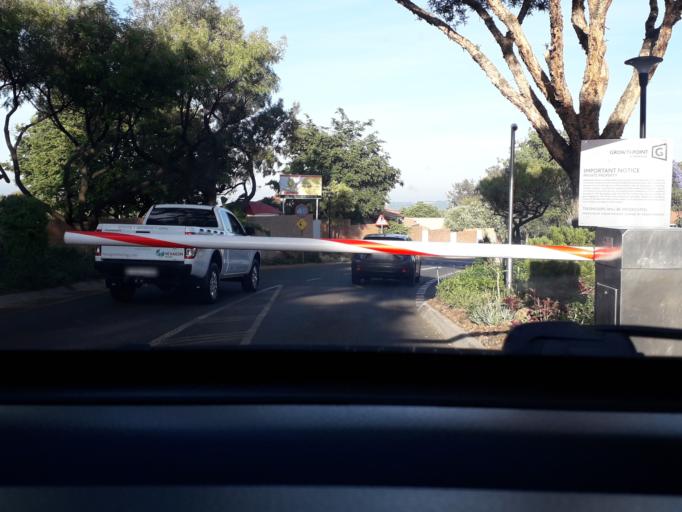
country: ZA
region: Gauteng
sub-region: City of Johannesburg Metropolitan Municipality
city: Modderfontein
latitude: -26.0630
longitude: 28.0895
